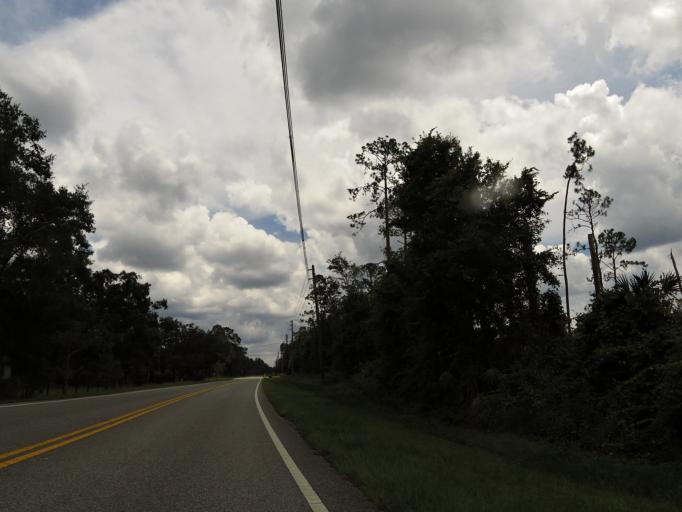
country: US
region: Florida
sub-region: Saint Johns County
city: Saint Augustine Shores
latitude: 29.6692
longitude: -81.4171
